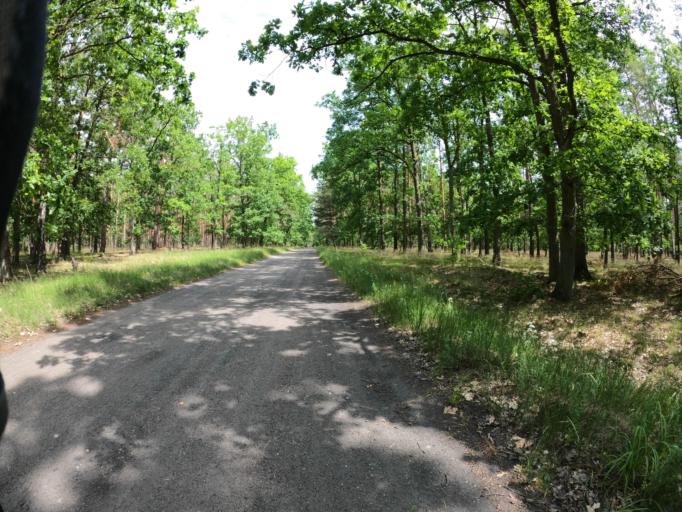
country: PL
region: West Pomeranian Voivodeship
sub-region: Powiat mysliborski
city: Boleszkowice
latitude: 52.6911
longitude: 14.5006
